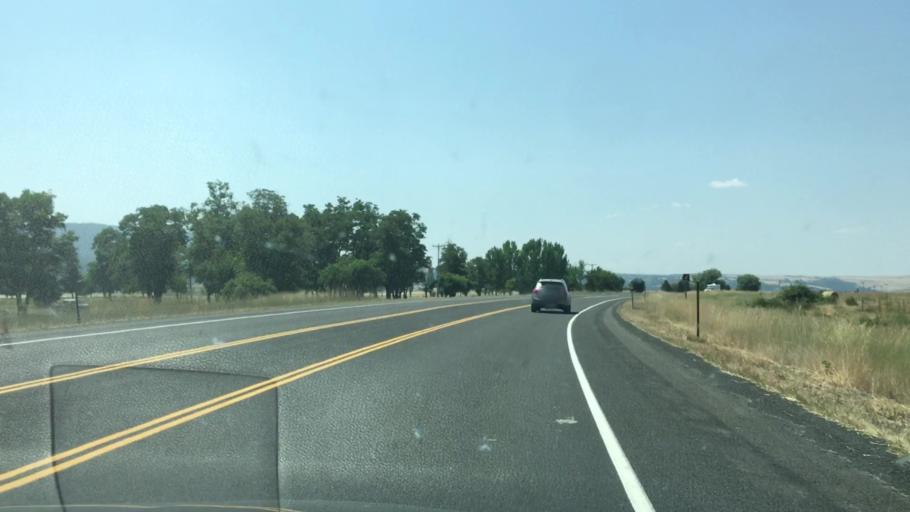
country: US
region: Idaho
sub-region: Idaho County
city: Grangeville
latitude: 45.9146
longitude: -116.1592
